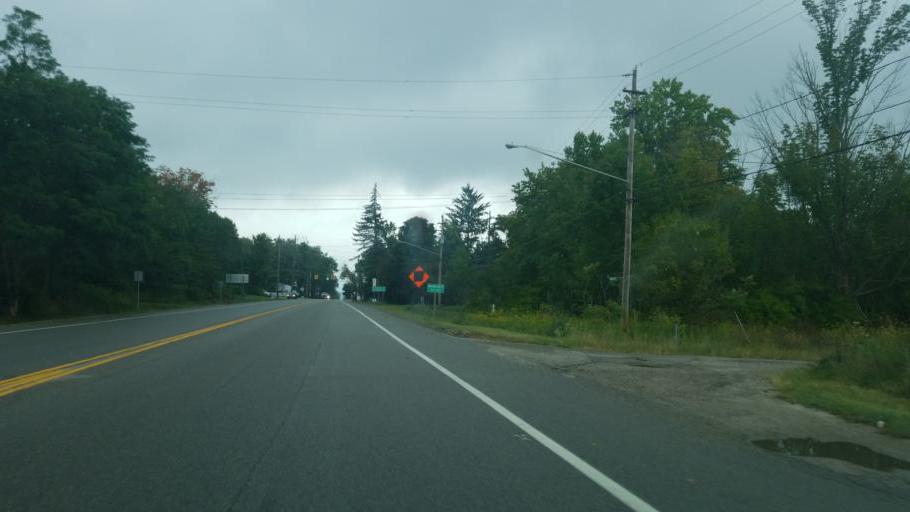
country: US
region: Ohio
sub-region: Portage County
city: Mantua
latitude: 41.3855
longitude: -81.2166
